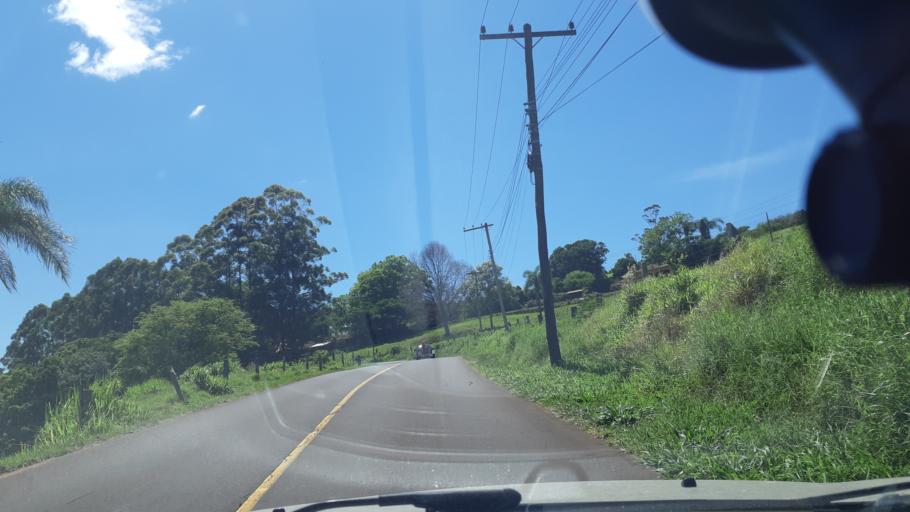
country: BR
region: Rio Grande do Sul
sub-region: Novo Hamburgo
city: Novo Hamburgo
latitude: -29.6270
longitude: -51.1063
